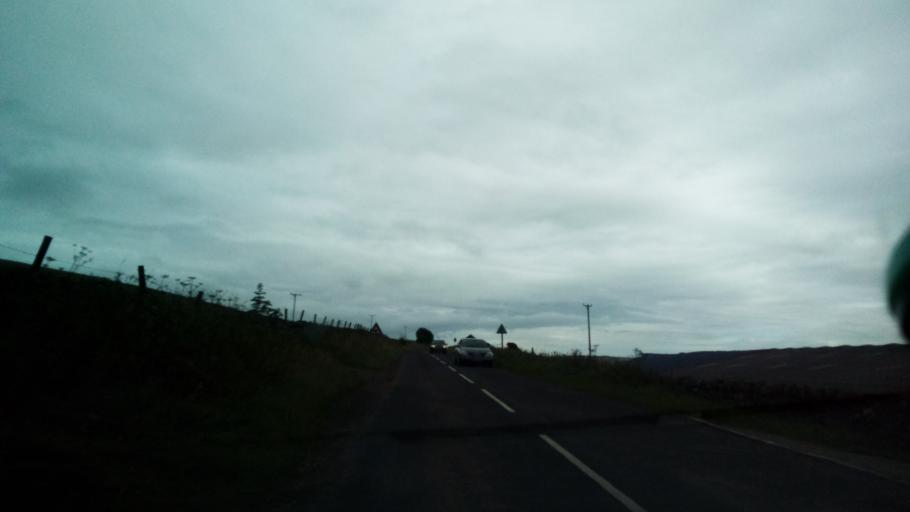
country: GB
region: England
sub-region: County Durham
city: Holwick
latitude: 54.5918
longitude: -2.1534
